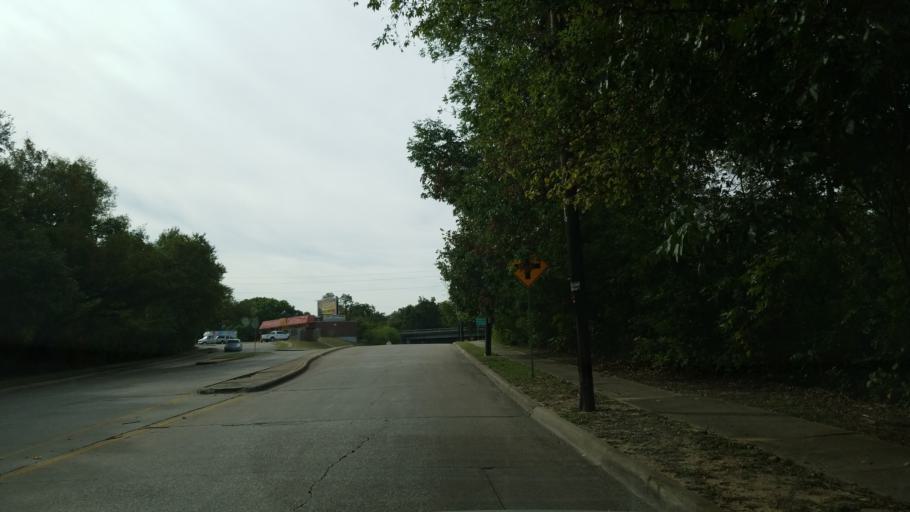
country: US
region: Texas
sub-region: Dallas County
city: Dallas
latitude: 32.7785
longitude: -96.7176
